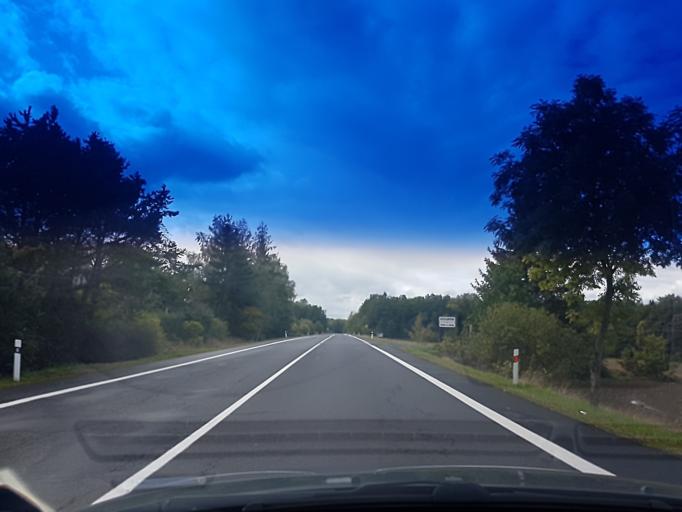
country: CZ
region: Karlovarsky
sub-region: Okres Cheb
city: Frantiskovy Lazne
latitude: 50.0812
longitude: 12.3258
